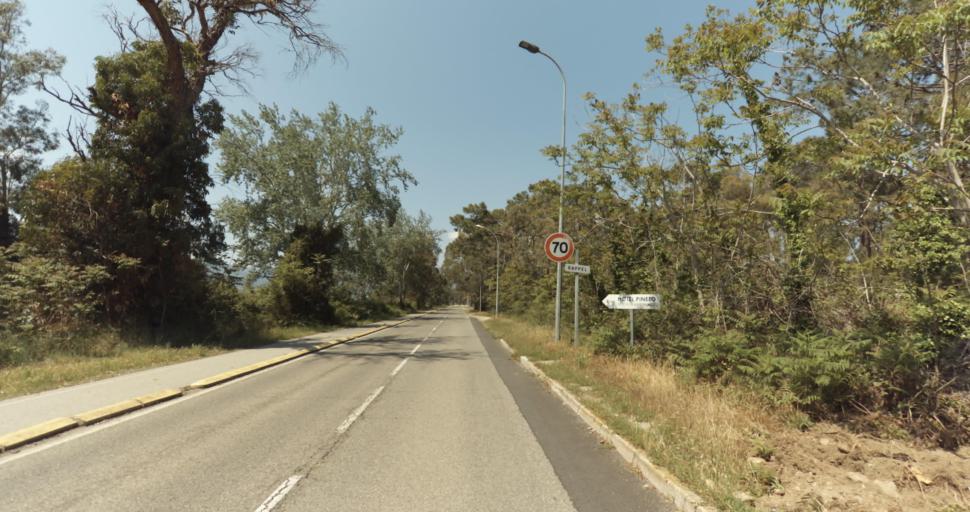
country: FR
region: Corsica
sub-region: Departement de la Haute-Corse
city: Biguglia
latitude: 42.6168
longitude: 9.4775
